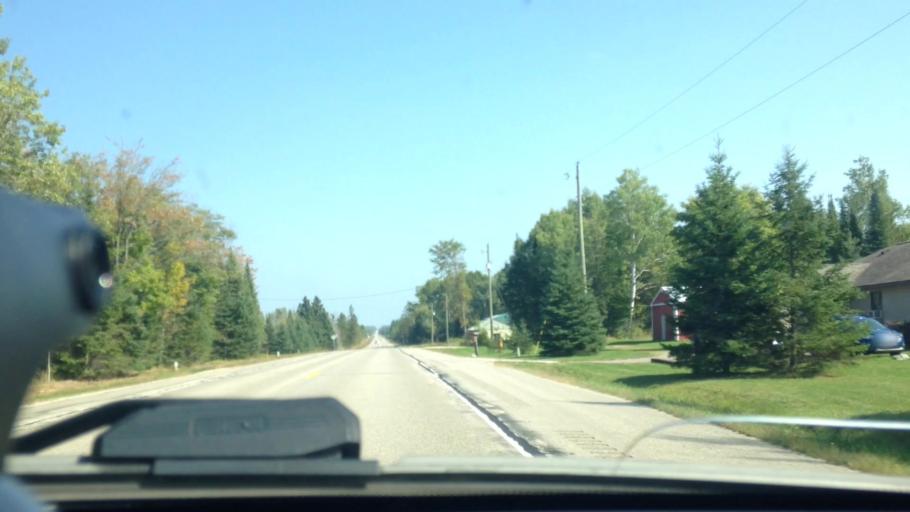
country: US
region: Michigan
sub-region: Luce County
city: Newberry
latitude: 46.3034
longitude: -85.3496
